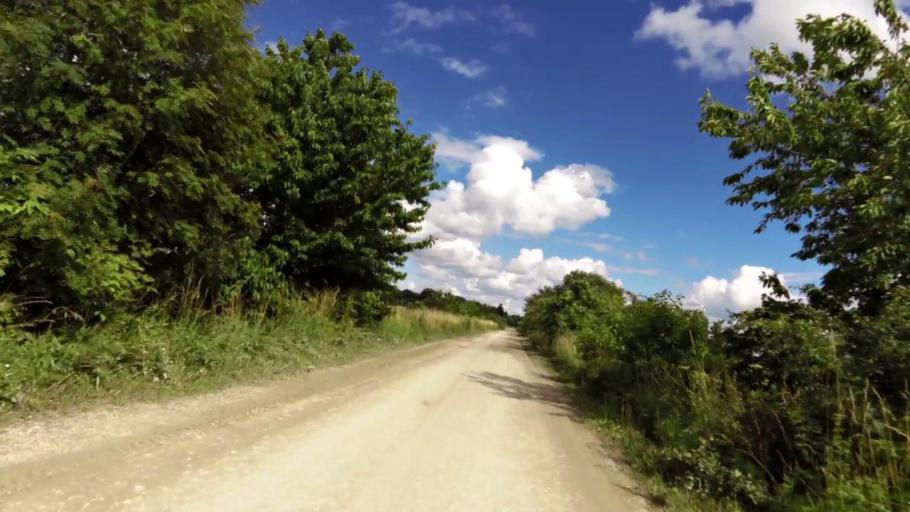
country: PL
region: Pomeranian Voivodeship
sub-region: Powiat slupski
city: Ustka
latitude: 54.5165
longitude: 16.7244
